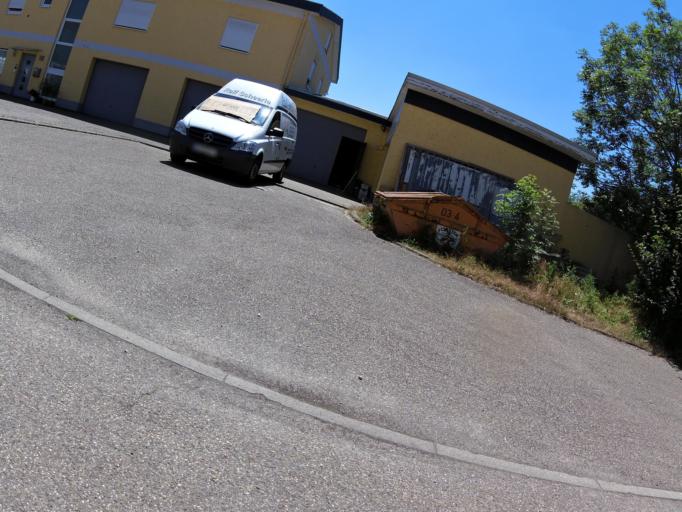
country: DE
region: Baden-Wuerttemberg
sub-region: Freiburg Region
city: Lahr
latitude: 48.3389
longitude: 7.8300
